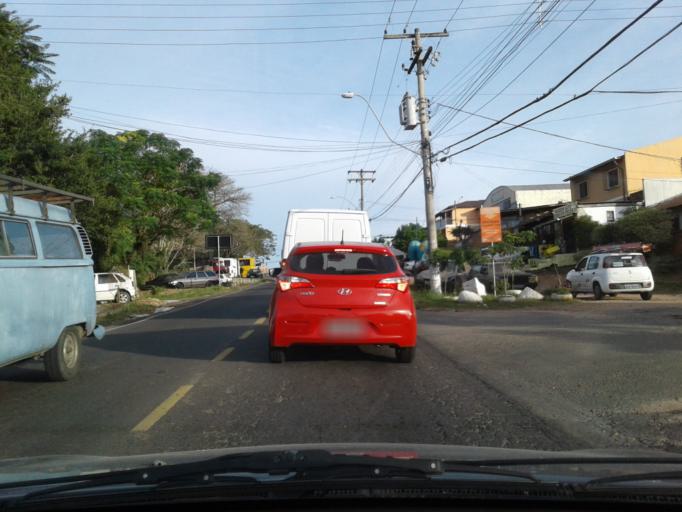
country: BR
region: Rio Grande do Sul
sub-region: Porto Alegre
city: Porto Alegre
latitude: -30.1060
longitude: -51.2225
